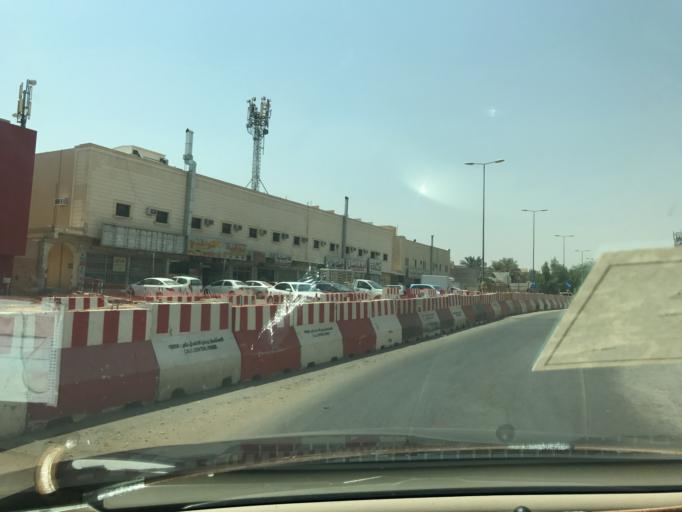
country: SA
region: Ar Riyad
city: Riyadh
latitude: 24.7481
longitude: 46.7735
